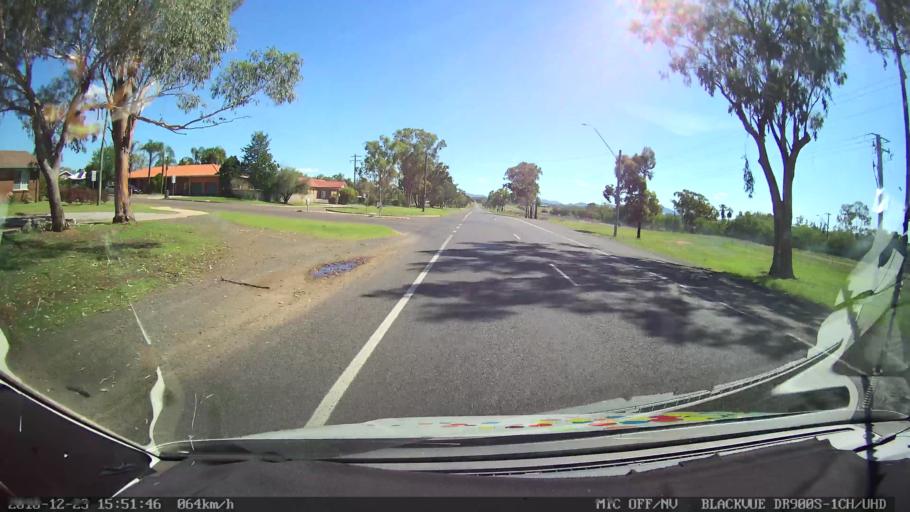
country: AU
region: New South Wales
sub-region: Tamworth Municipality
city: South Tamworth
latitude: -31.1151
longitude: 150.8942
